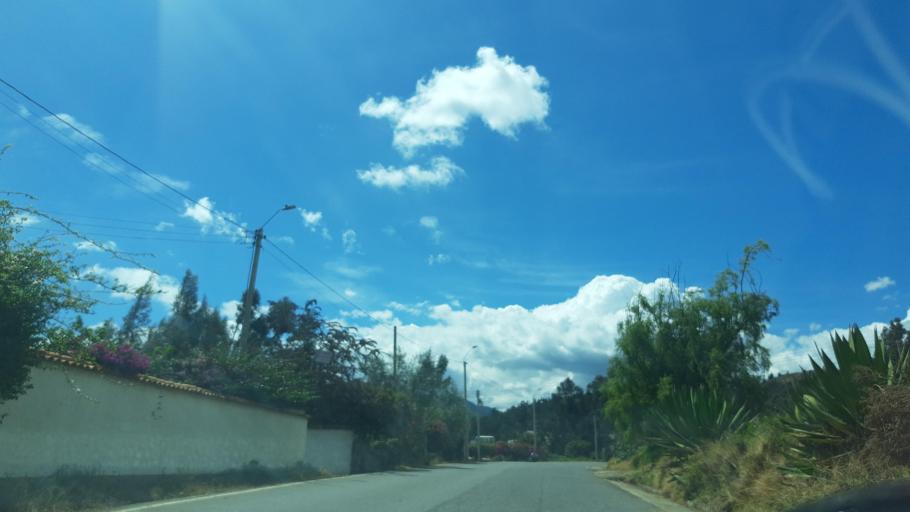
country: CO
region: Boyaca
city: Cucaita
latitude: 5.5387
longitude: -73.4986
